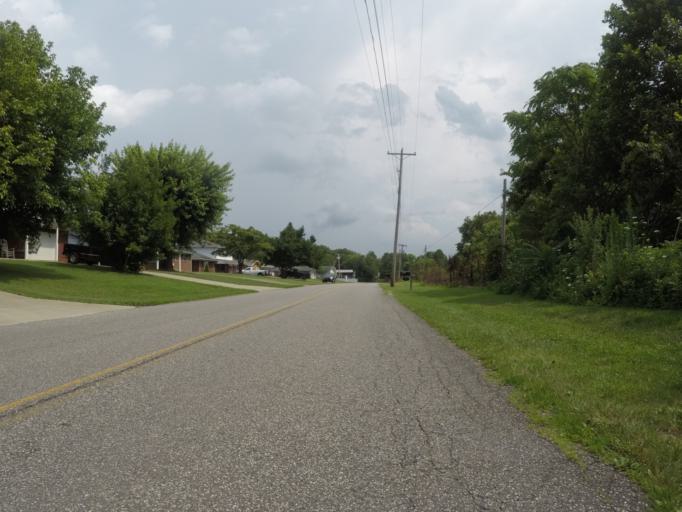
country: US
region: Kentucky
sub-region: Boyd County
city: Ironville
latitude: 38.4388
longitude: -82.7078
